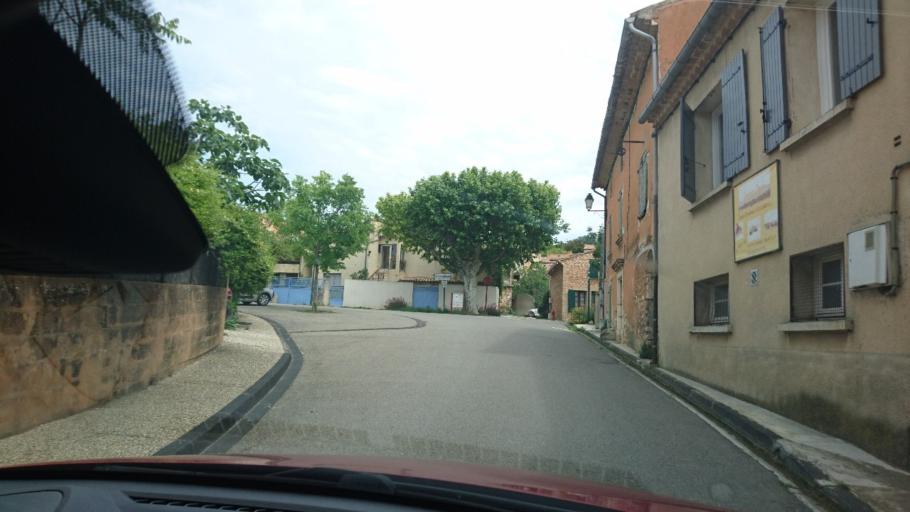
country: FR
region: Provence-Alpes-Cote d'Azur
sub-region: Departement du Vaucluse
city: Villes-sur-Auzon
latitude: 44.0982
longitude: 5.2413
